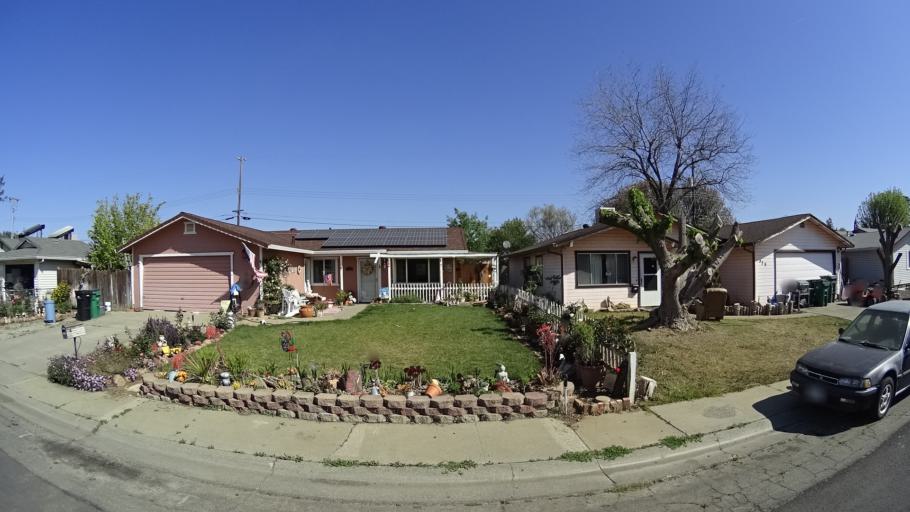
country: US
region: California
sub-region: Glenn County
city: Willows
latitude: 39.5310
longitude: -122.2001
